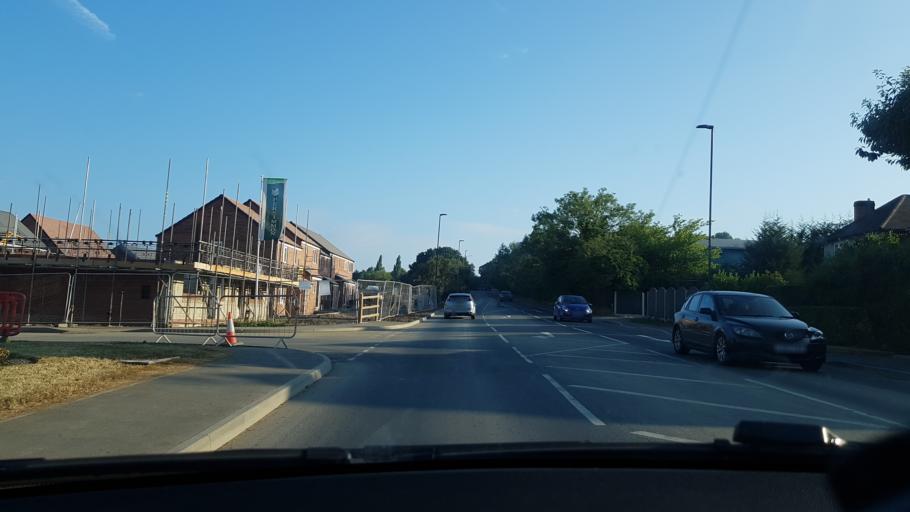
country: GB
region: England
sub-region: Derbyshire
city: Ilkeston
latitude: 52.9544
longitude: -1.3073
